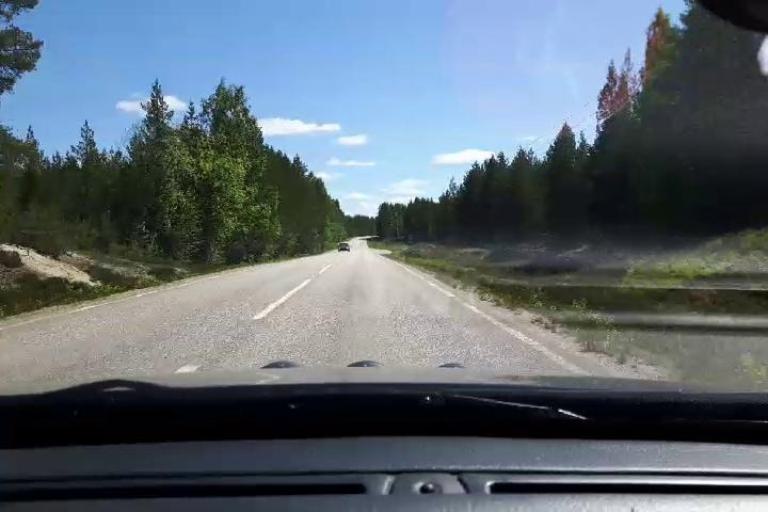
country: SE
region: Vaesternorrland
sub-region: Ange Kommun
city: Ange
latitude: 62.0936
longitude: 15.0862
